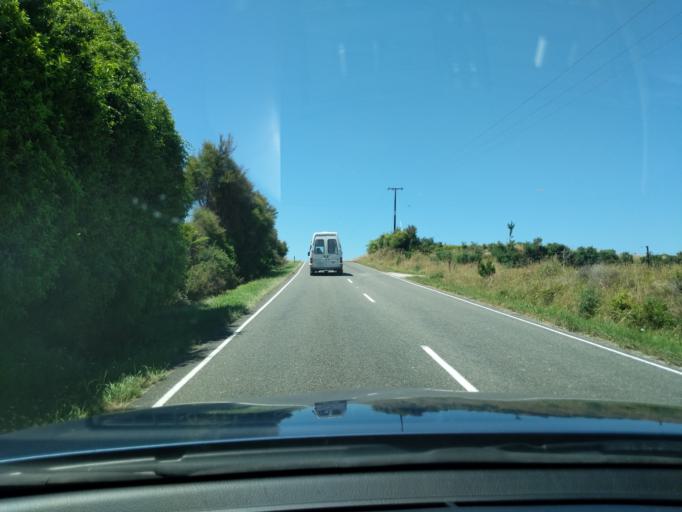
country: NZ
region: Tasman
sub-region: Tasman District
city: Takaka
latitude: -40.6934
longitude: 172.6404
